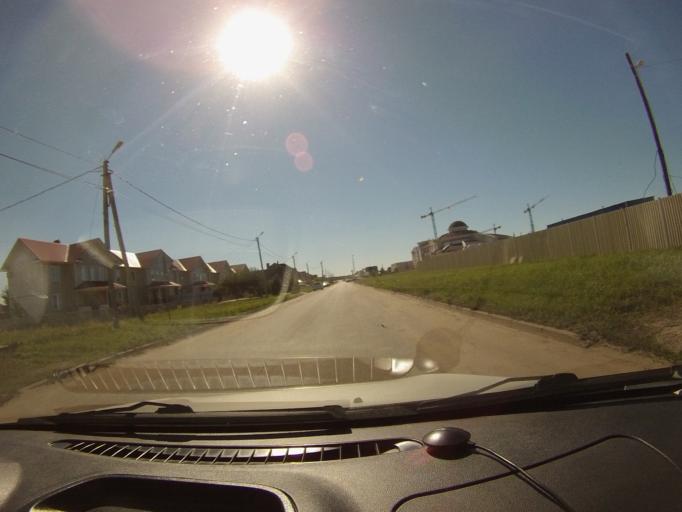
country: RU
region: Tambov
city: Tambov
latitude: 52.7703
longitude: 41.3860
